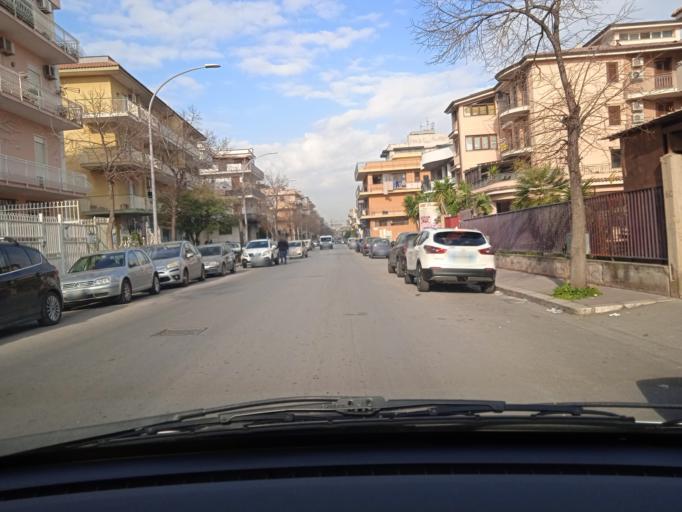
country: IT
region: Sicily
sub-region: Palermo
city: Villabate
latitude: 38.0779
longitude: 13.4471
